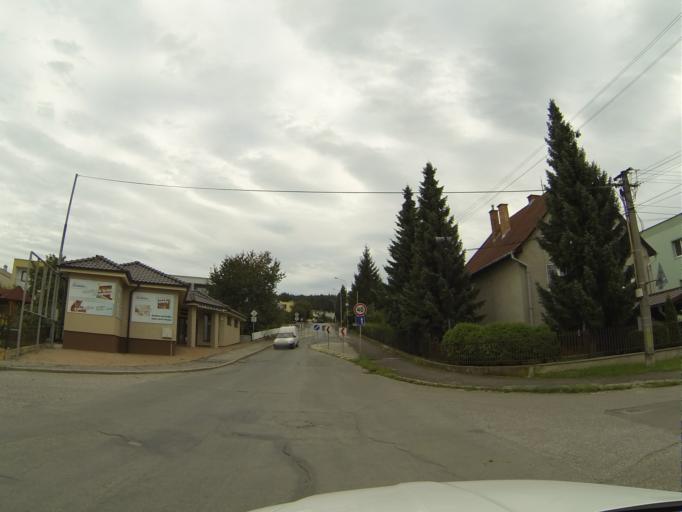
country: SK
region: Nitriansky
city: Prievidza
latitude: 48.7876
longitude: 18.6380
